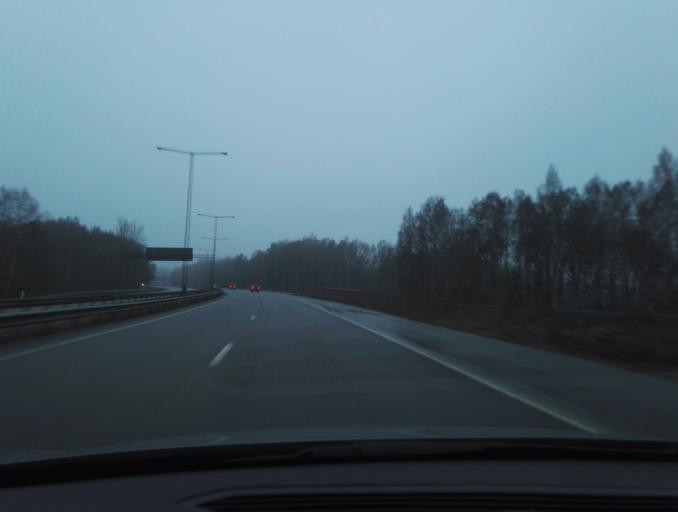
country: SE
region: Kronoberg
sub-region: Vaxjo Kommun
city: Vaexjoe
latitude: 56.8908
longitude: 14.7523
